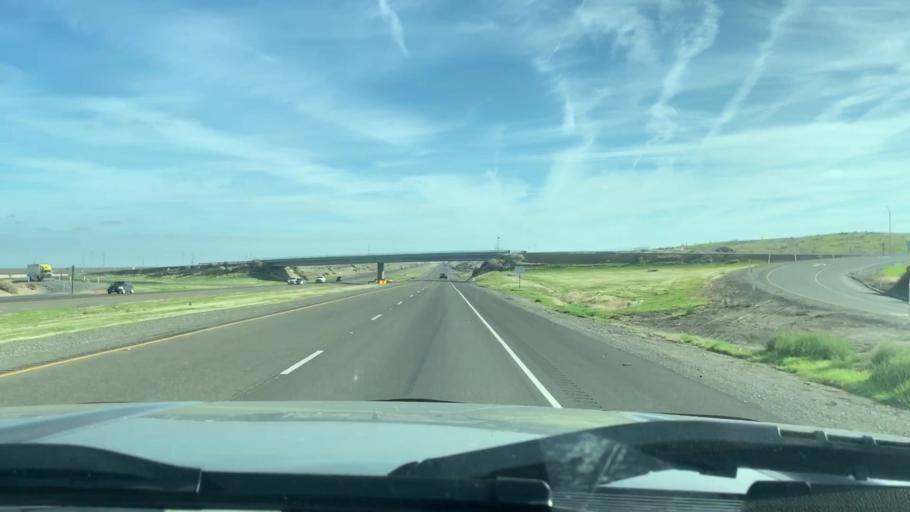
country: US
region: California
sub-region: Fresno County
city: Mendota
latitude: 36.5319
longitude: -120.4900
